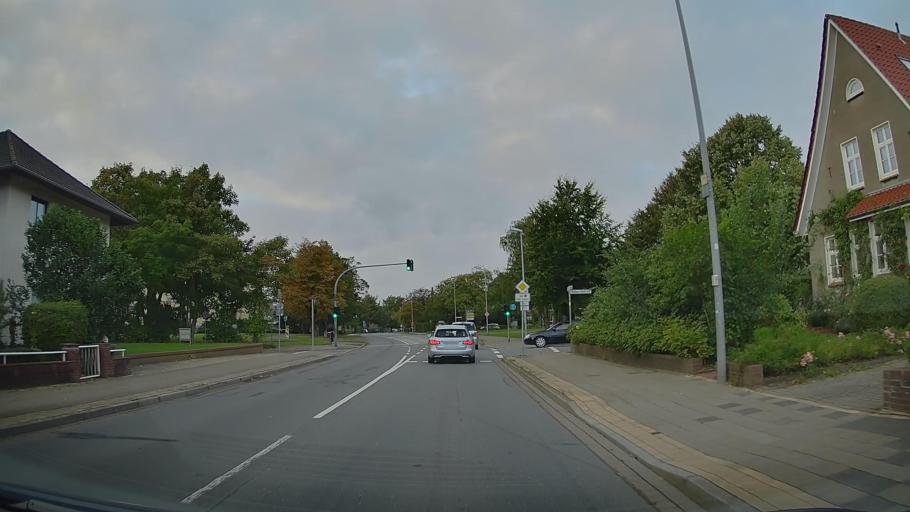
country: DE
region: Schleswig-Holstein
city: Husum
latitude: 54.4824
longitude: 9.0551
